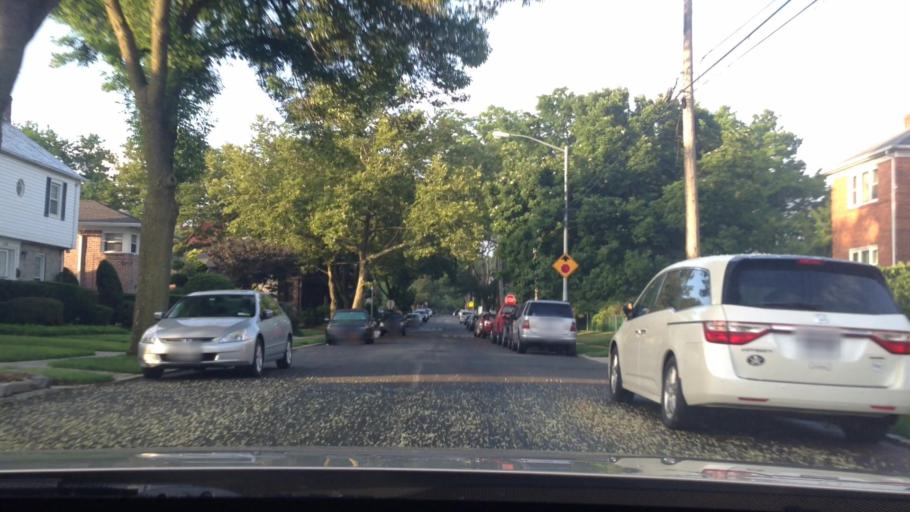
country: US
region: New York
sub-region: Nassau County
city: East Atlantic Beach
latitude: 40.7694
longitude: -73.7943
